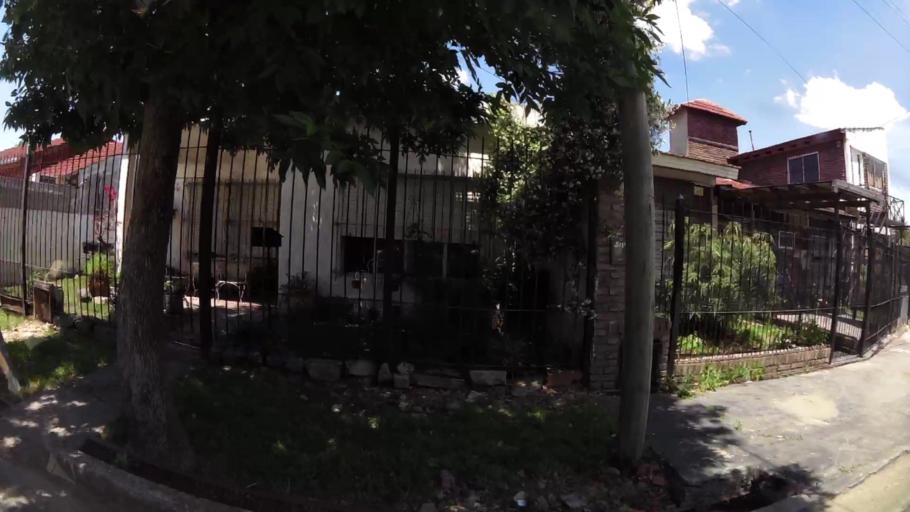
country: AR
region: Buenos Aires
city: Ituzaingo
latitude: -34.6590
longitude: -58.6905
